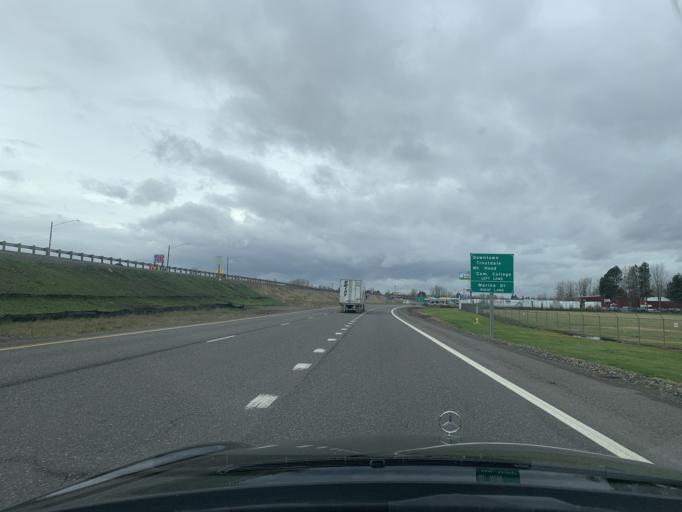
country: US
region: Oregon
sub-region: Multnomah County
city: Troutdale
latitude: 45.5457
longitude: -122.3932
